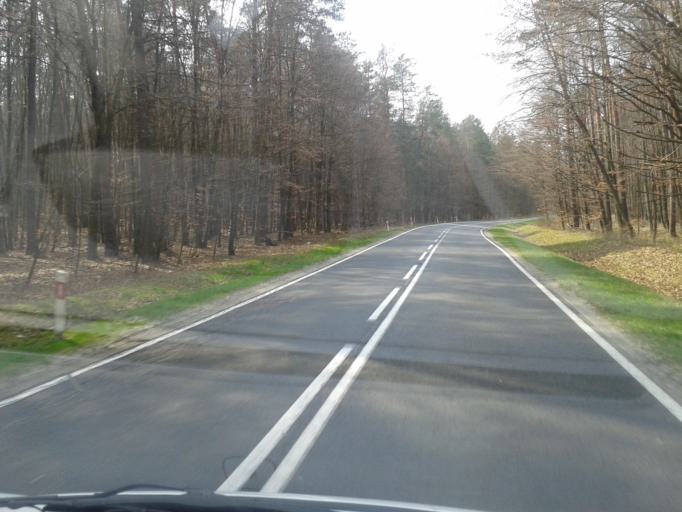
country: PL
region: Subcarpathian Voivodeship
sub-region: Powiat lubaczowski
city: Narol
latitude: 50.3417
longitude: 23.3109
